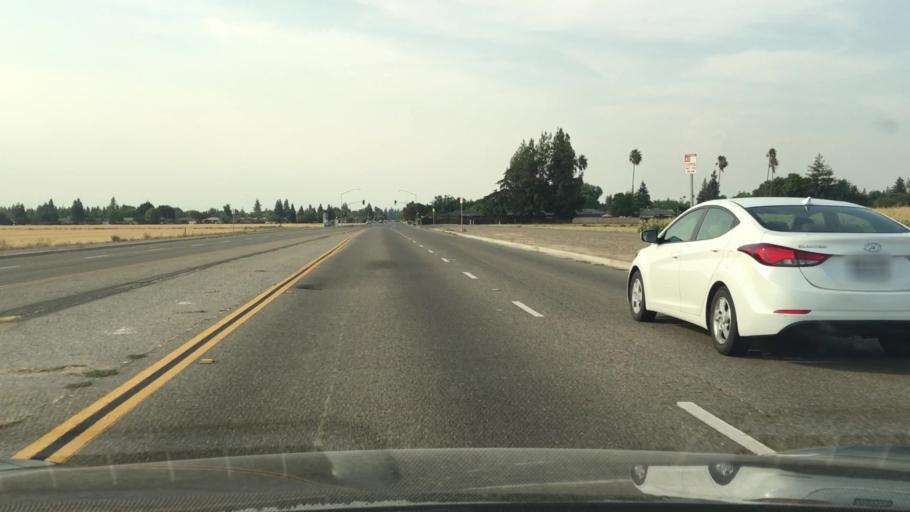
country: US
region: California
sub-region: Fresno County
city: Clovis
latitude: 36.8243
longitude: -119.7360
